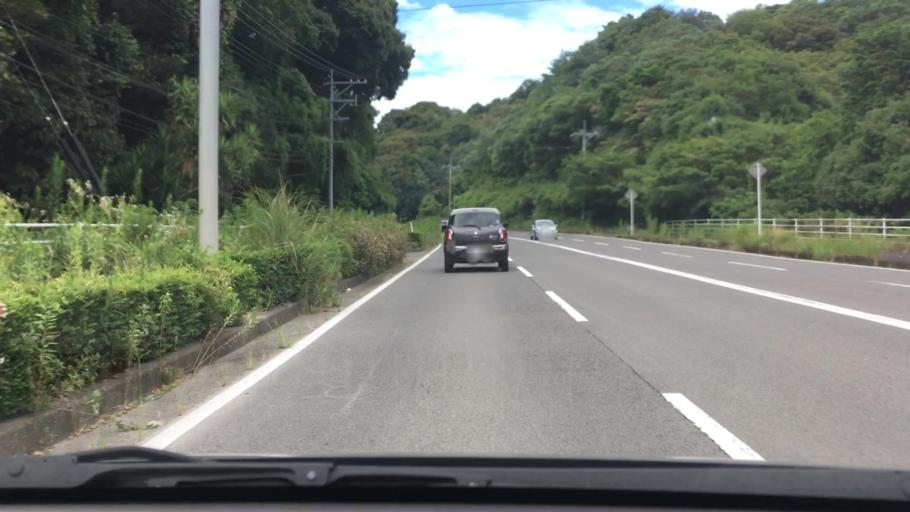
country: JP
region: Nagasaki
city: Sasebo
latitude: 32.9887
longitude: 129.7483
